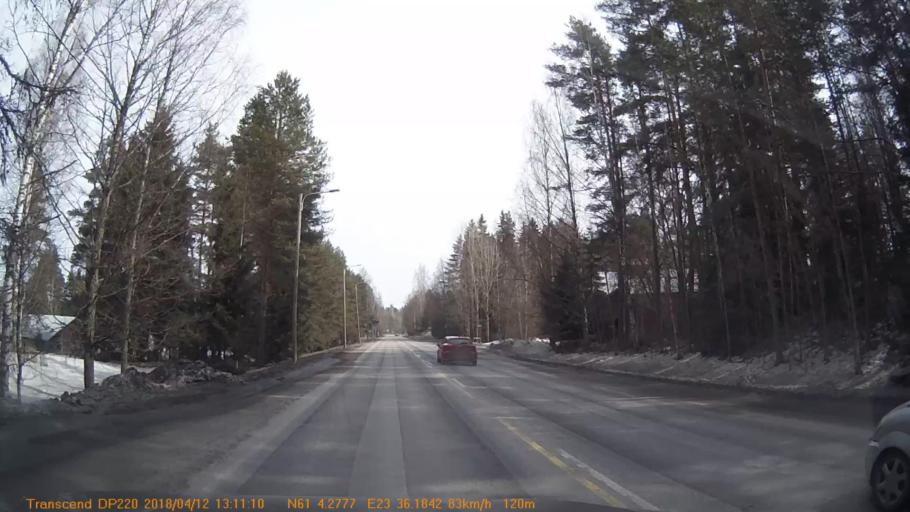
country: FI
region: Pirkanmaa
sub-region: Etelae-Pirkanmaa
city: Urjala
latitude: 61.0713
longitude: 23.6047
